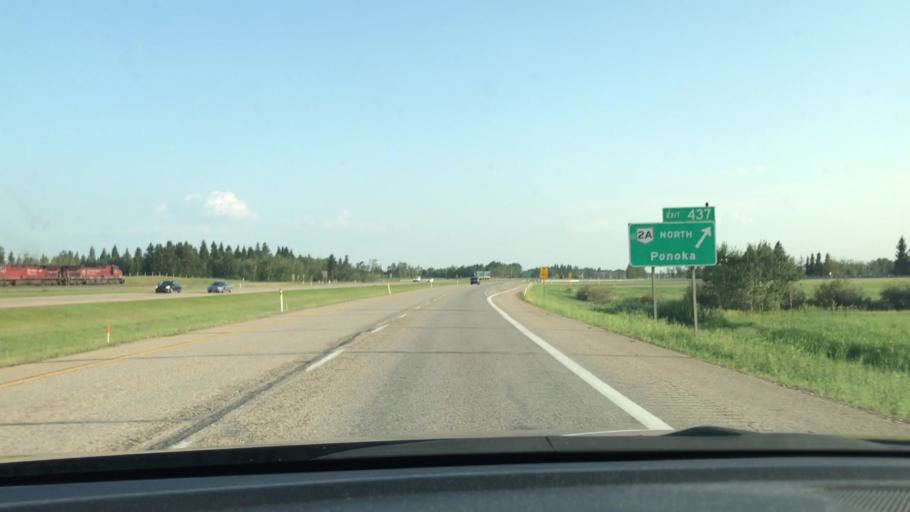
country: CA
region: Alberta
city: Lacombe
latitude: 52.5578
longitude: -113.6632
